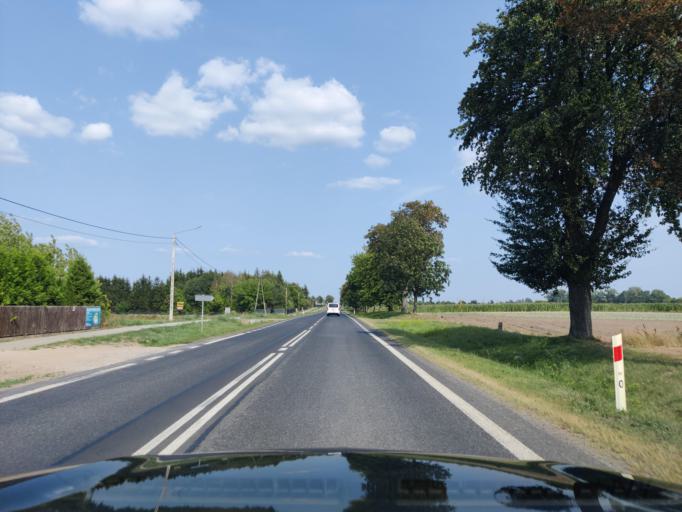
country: PL
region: Masovian Voivodeship
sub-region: Powiat makowski
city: Rozan
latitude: 52.8822
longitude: 21.3765
